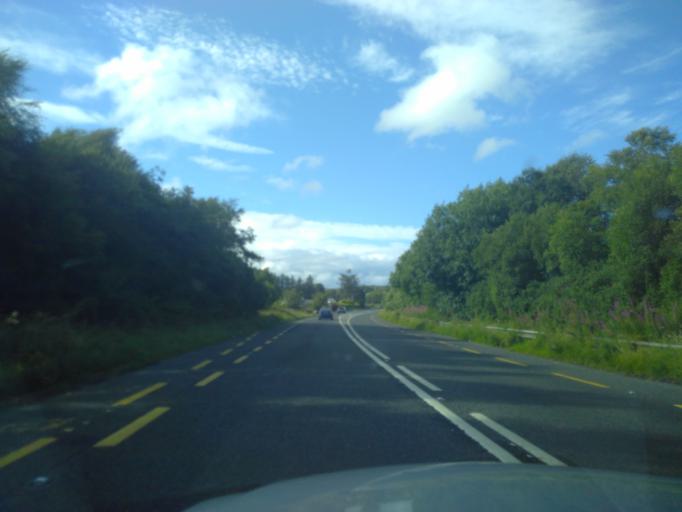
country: IE
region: Ulster
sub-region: County Donegal
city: Ballybofey
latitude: 54.8433
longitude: -7.7509
